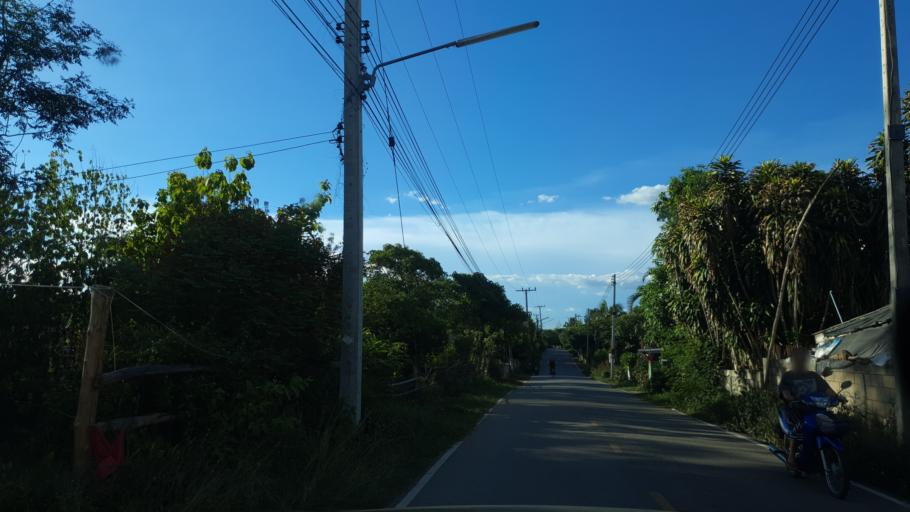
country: TH
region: Lampang
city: Sop Prap
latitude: 17.8887
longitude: 99.3113
